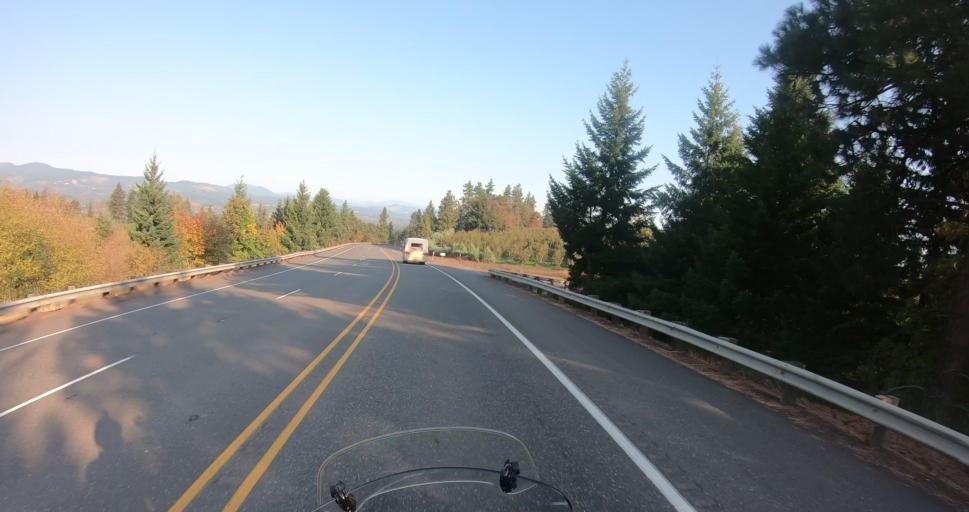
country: US
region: Oregon
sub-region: Hood River County
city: Odell
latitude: 45.6163
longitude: -121.5308
